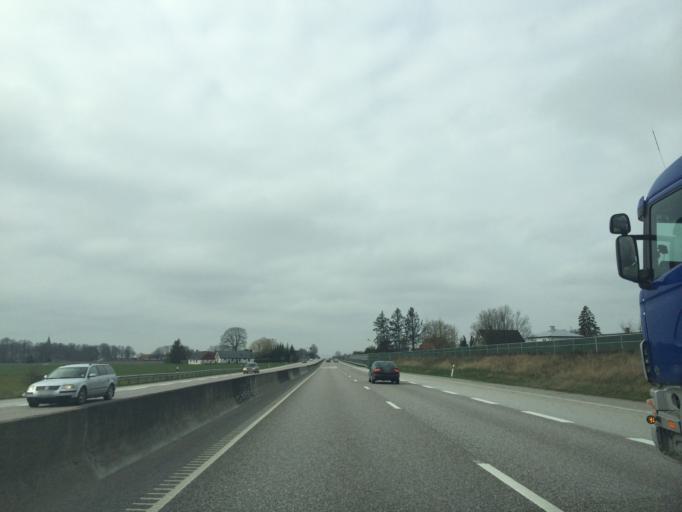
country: SE
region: Skane
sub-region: Lunds Kommun
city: Lund
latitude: 55.6753
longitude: 13.1767
